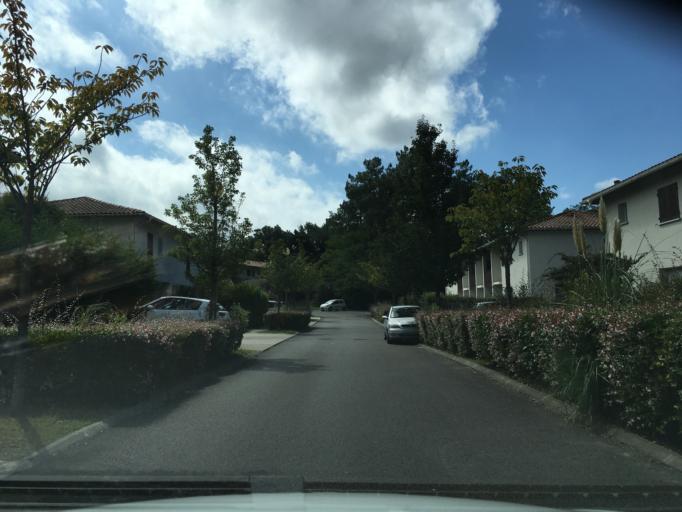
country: FR
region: Aquitaine
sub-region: Departement des Pyrenees-Atlantiques
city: Boucau
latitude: 43.4984
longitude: -1.4500
